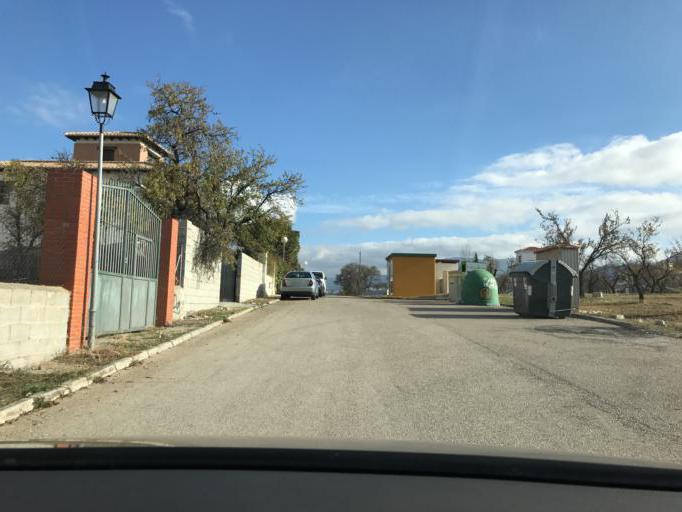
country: ES
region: Andalusia
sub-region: Provincia de Granada
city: Otura
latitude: 37.0842
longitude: -3.6249
